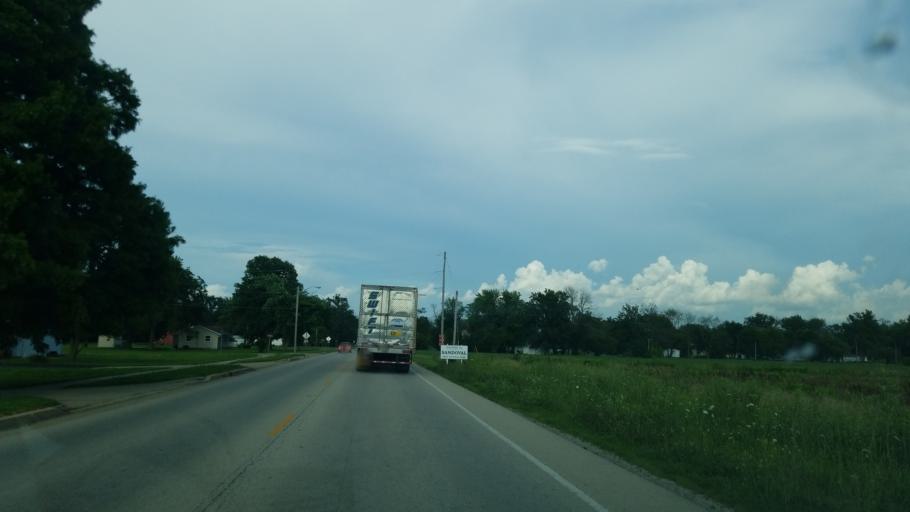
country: US
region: Illinois
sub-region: Marion County
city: Sandoval
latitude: 38.6163
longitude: -89.1290
